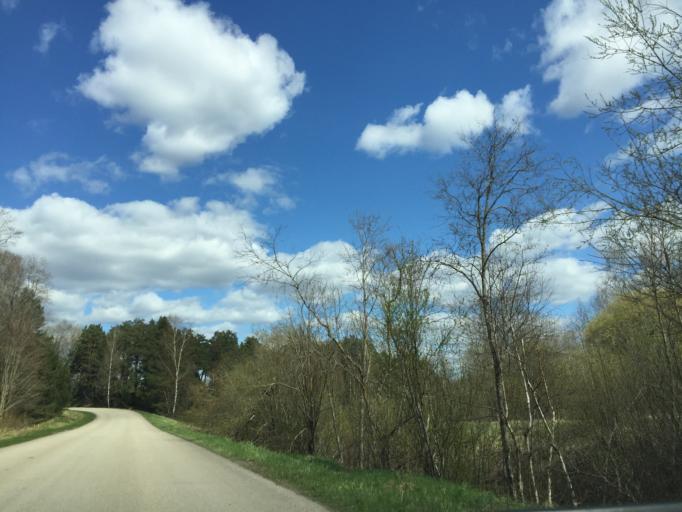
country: LV
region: Rezekne
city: Rezekne
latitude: 56.5449
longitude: 27.1483
